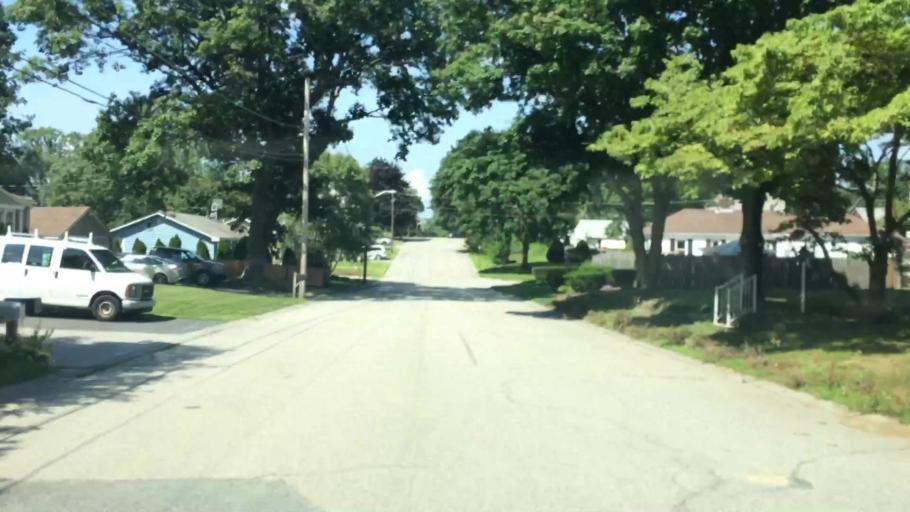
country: US
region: Rhode Island
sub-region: Providence County
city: Cumberland Hill
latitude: 41.9856
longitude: -71.4871
